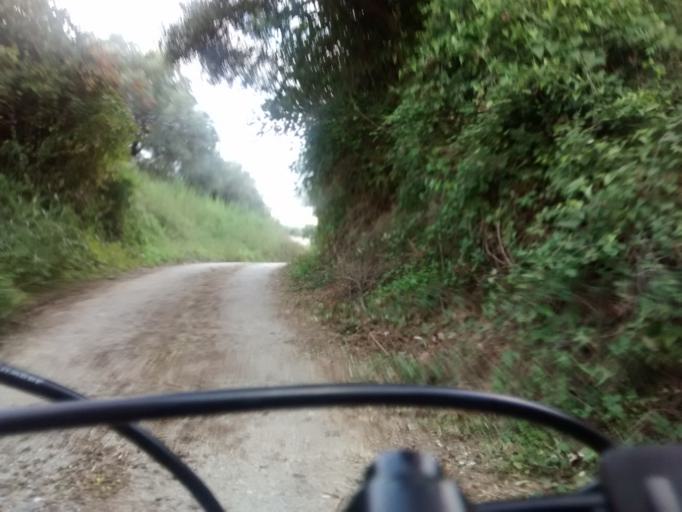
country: IT
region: Calabria
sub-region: Provincia di Catanzaro
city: Maida
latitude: 38.8914
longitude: 16.3583
